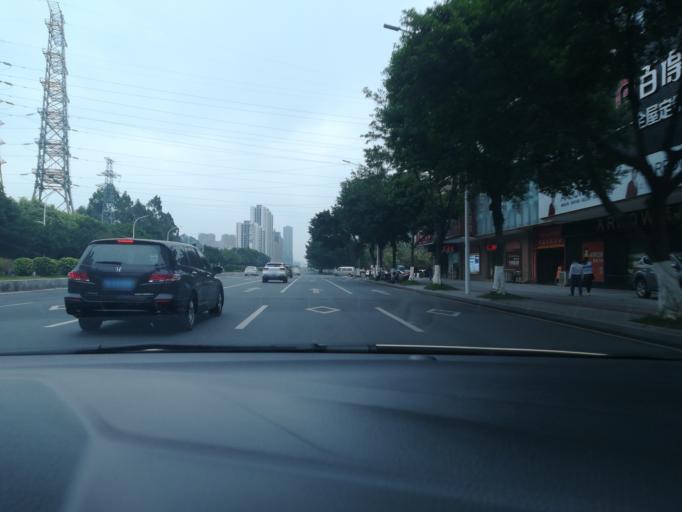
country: CN
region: Guangdong
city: Nansha
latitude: 22.8006
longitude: 113.5572
